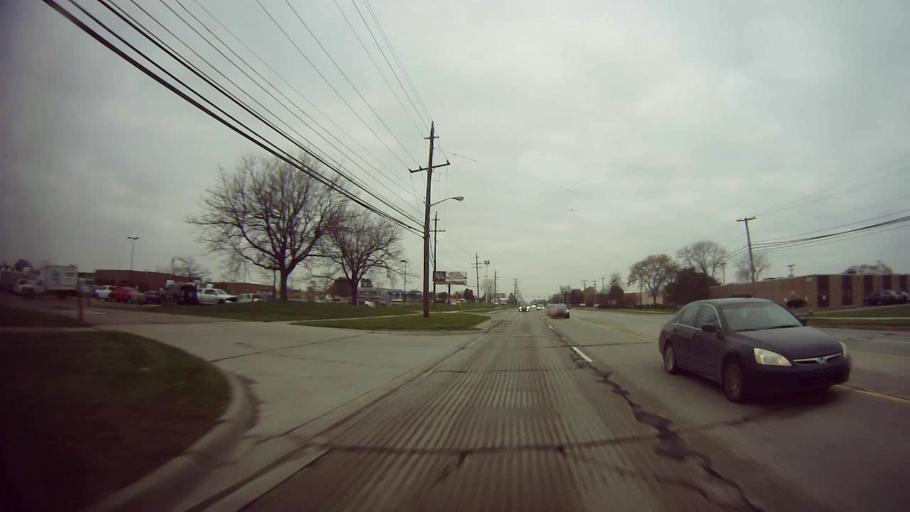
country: US
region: Michigan
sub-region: Oakland County
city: Madison Heights
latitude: 42.5322
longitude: -83.0867
